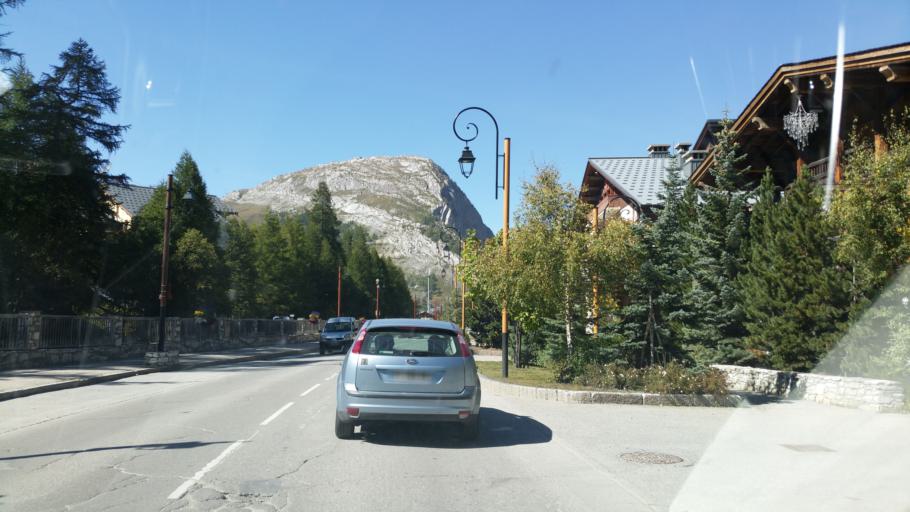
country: FR
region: Rhone-Alpes
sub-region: Departement de la Savoie
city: Val-d'Isere
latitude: 45.4515
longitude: 6.9751
